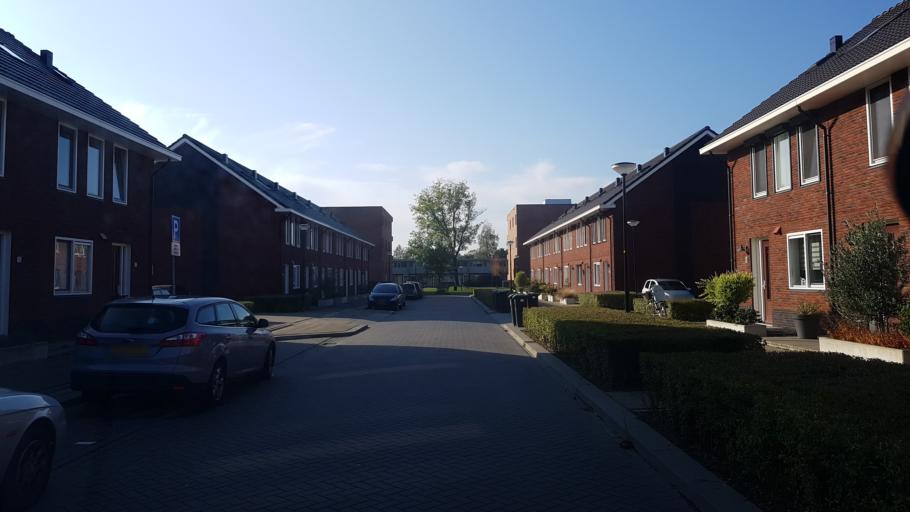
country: NL
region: Gelderland
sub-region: Gemeente Apeldoorn
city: Apeldoorn
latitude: 52.2328
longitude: 5.9836
